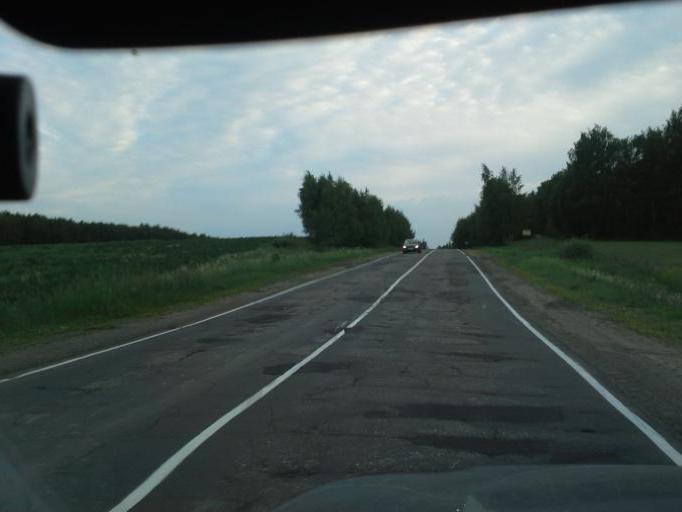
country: RU
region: Ivanovo
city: Petrovskiy
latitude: 56.5991
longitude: 40.2419
